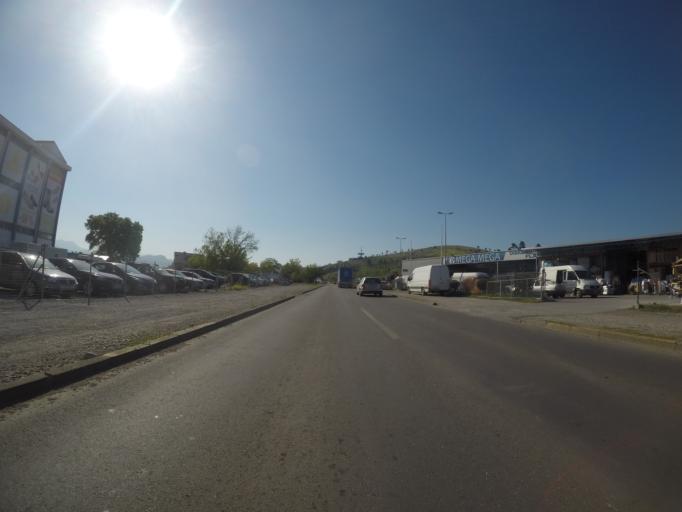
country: ME
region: Podgorica
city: Podgorica
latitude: 42.4265
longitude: 19.2339
